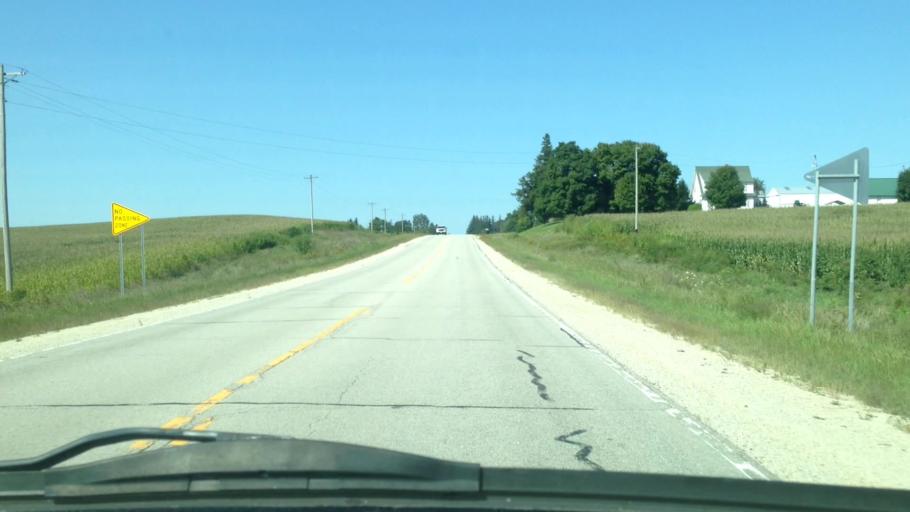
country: US
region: Minnesota
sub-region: Houston County
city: Spring Grove
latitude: 43.6106
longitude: -91.7904
